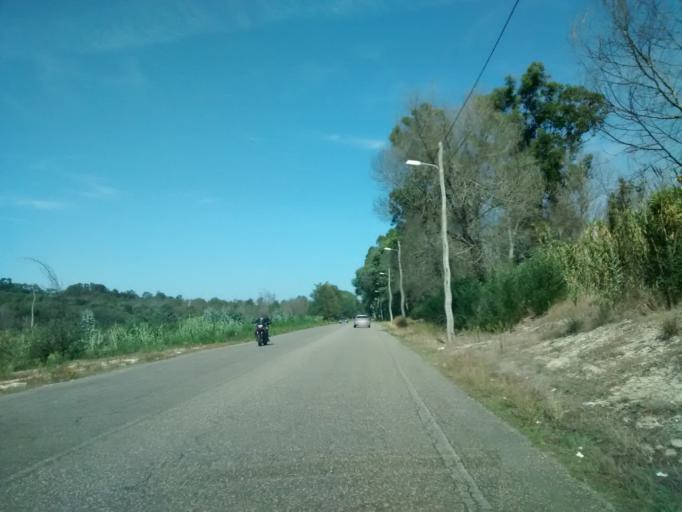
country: PT
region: Coimbra
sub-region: Mira
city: Mira
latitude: 40.4477
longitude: -8.7631
